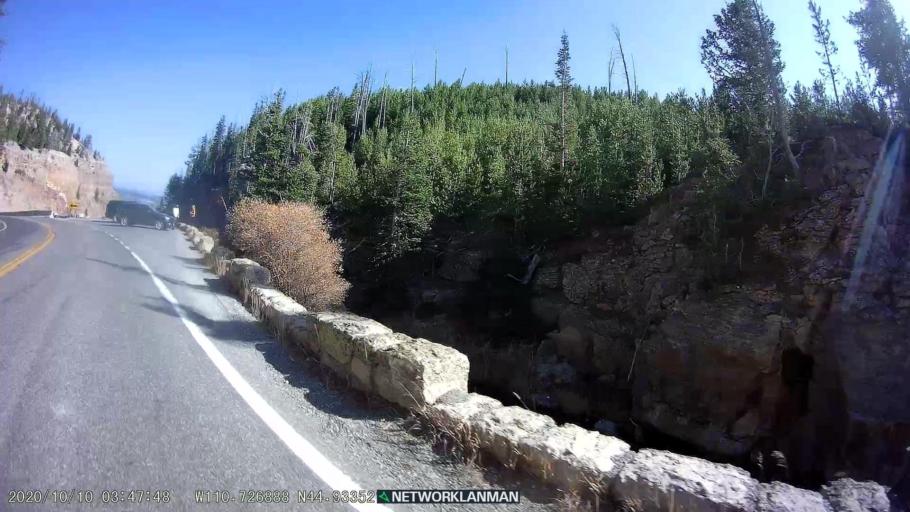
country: US
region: Montana
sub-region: Gallatin County
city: West Yellowstone
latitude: 44.9336
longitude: -110.7270
